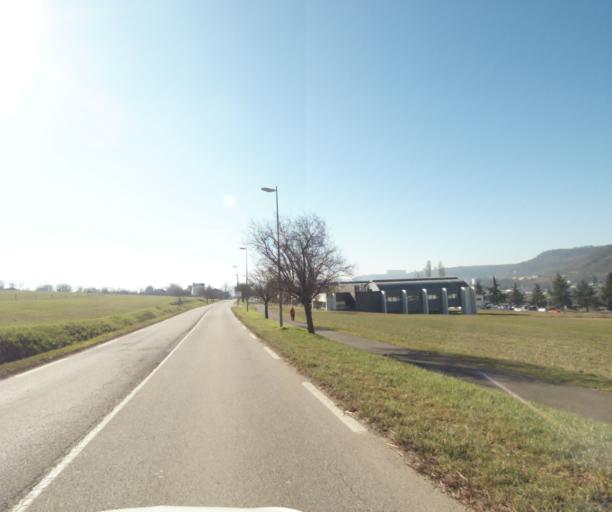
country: FR
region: Lorraine
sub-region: Departement de Meurthe-et-Moselle
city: Malzeville
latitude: 48.7287
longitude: 6.1823
